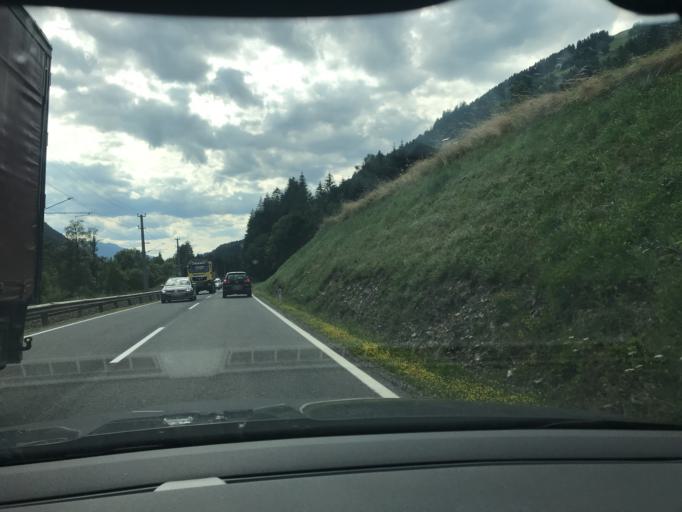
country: AT
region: Tyrol
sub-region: Politischer Bezirk Lienz
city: Anras
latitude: 46.7762
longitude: 12.6278
